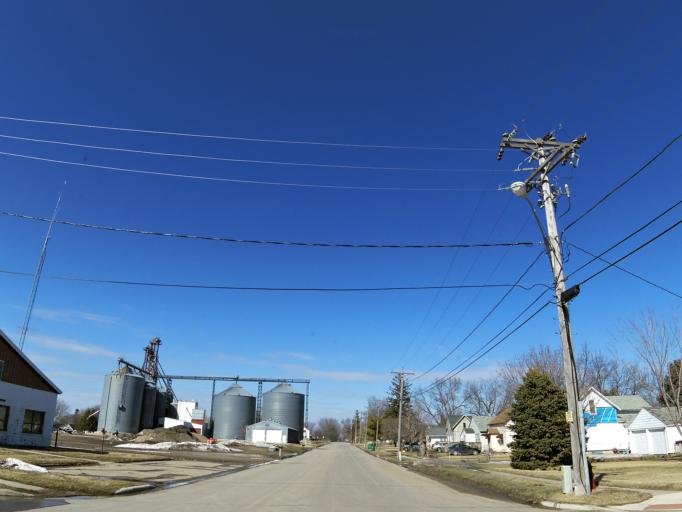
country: US
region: Minnesota
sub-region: Waseca County
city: New Richland
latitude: 43.8949
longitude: -93.4916
